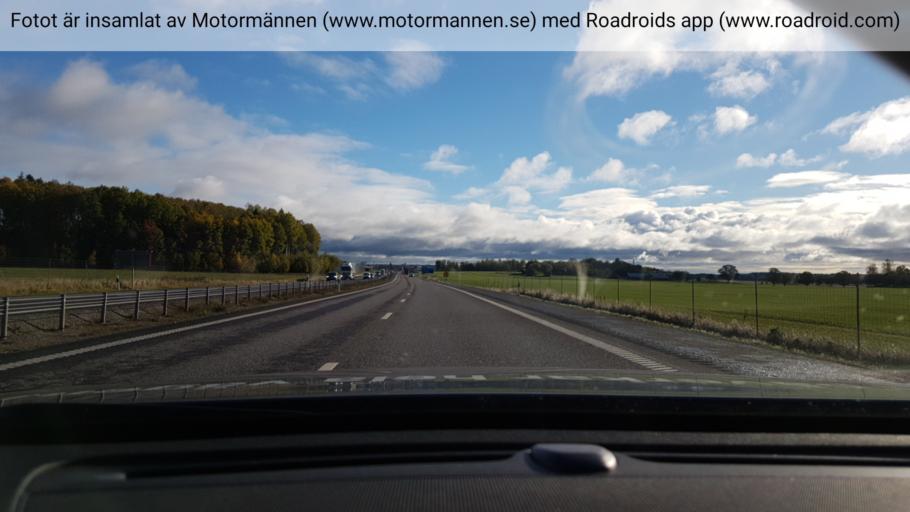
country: SE
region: Soedermanland
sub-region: Nykopings Kommun
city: Nykoping
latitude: 58.7461
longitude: 16.9457
